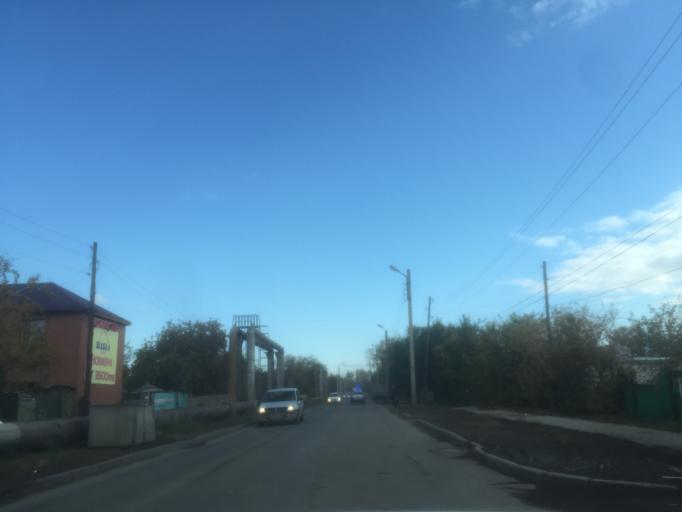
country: KZ
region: Astana Qalasy
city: Astana
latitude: 51.1919
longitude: 71.3954
